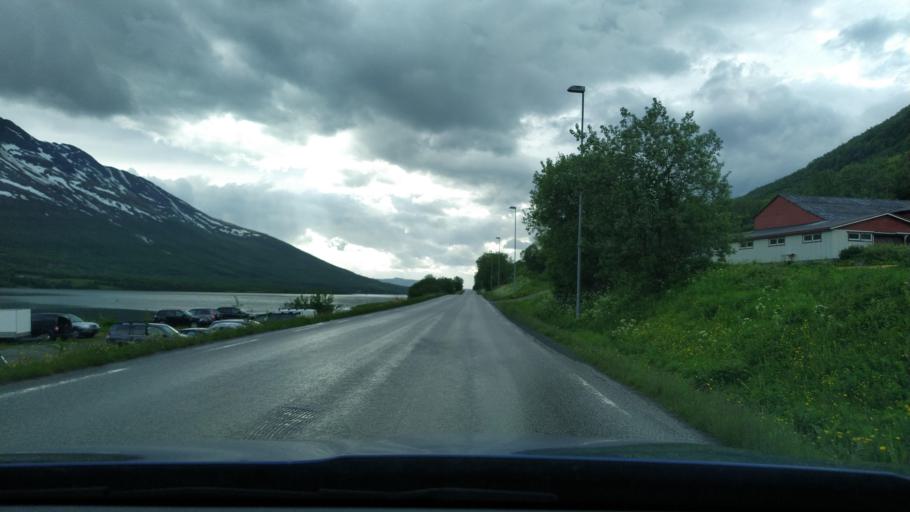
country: NO
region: Troms
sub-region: Balsfjord
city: Storsteinnes
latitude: 69.2203
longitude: 19.5366
